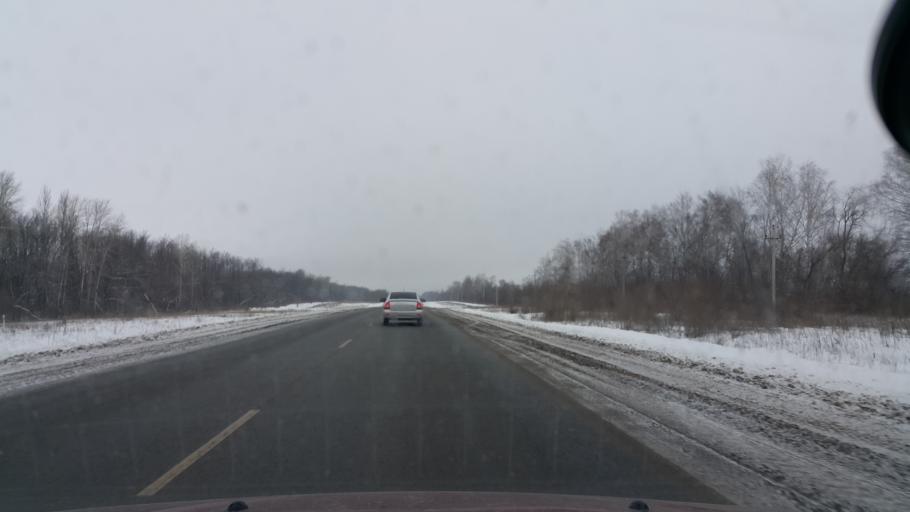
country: RU
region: Tambov
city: Bokino
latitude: 52.6045
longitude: 41.4435
